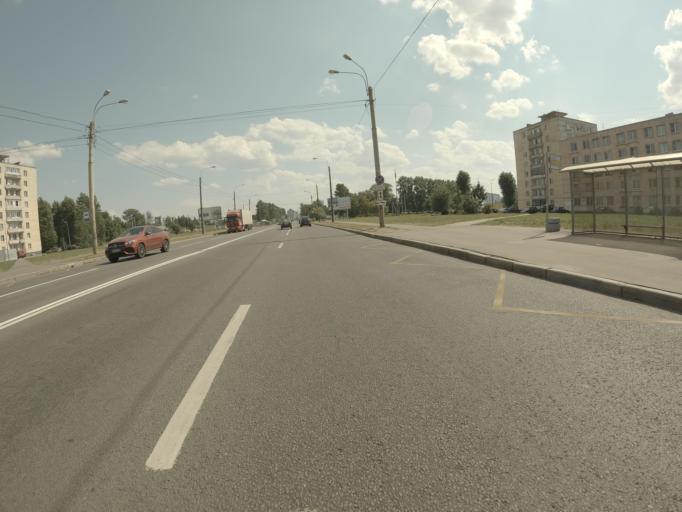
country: RU
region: St.-Petersburg
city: Avtovo
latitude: 59.8668
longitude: 30.2769
